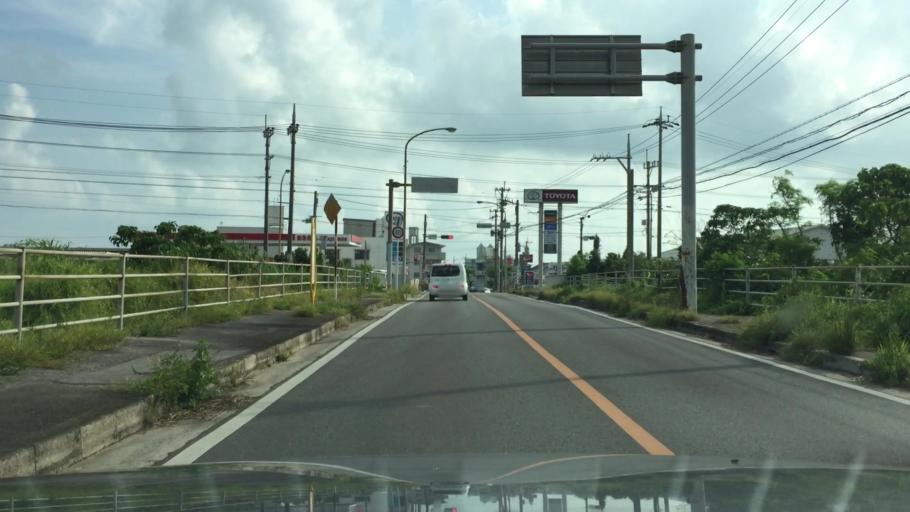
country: JP
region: Okinawa
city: Ishigaki
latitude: 24.3481
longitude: 124.1692
